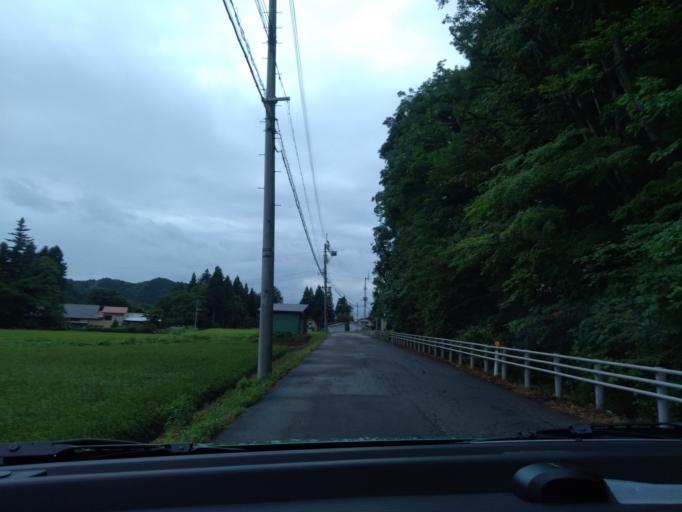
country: JP
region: Akita
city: Omagari
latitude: 39.4280
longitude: 140.6051
